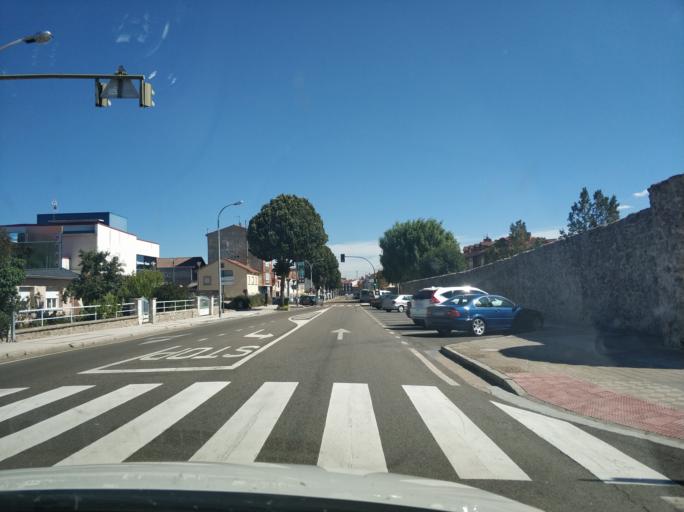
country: ES
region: Castille and Leon
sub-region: Provincia de Palencia
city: Aguilar de Campoo
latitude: 42.7954
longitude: -4.2604
